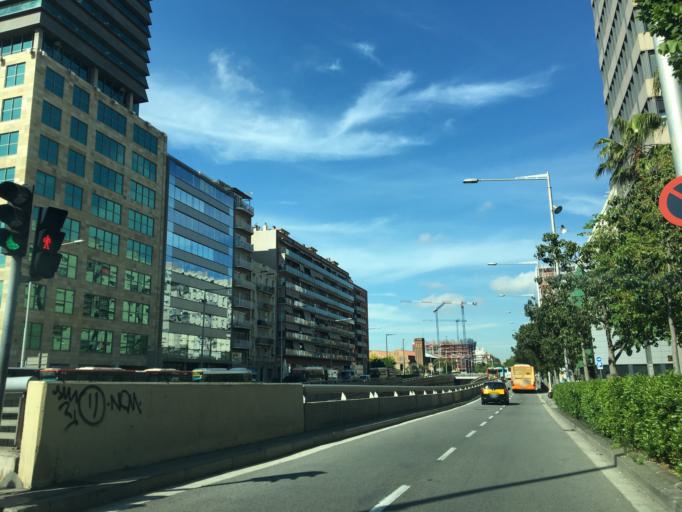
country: ES
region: Catalonia
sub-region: Provincia de Barcelona
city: Sants-Montjuic
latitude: 41.3650
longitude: 2.1360
